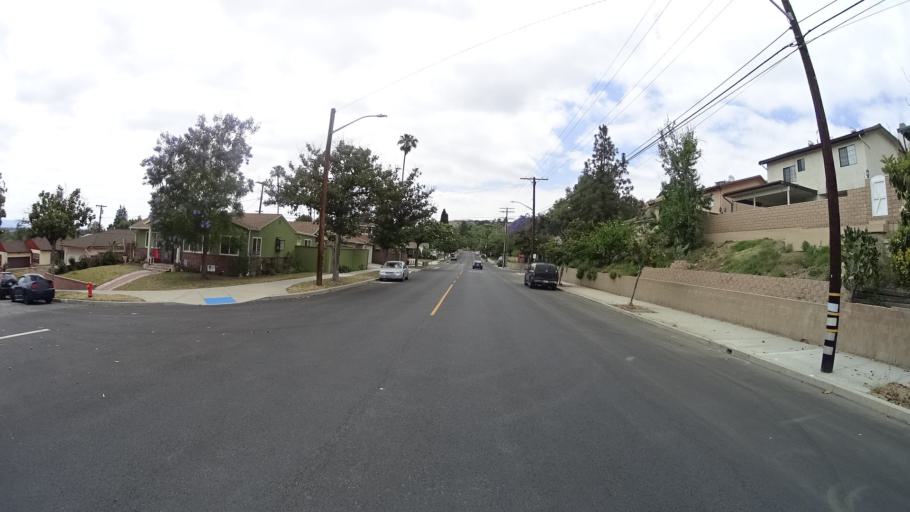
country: US
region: California
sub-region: Los Angeles County
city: Burbank
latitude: 34.2052
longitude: -118.3252
